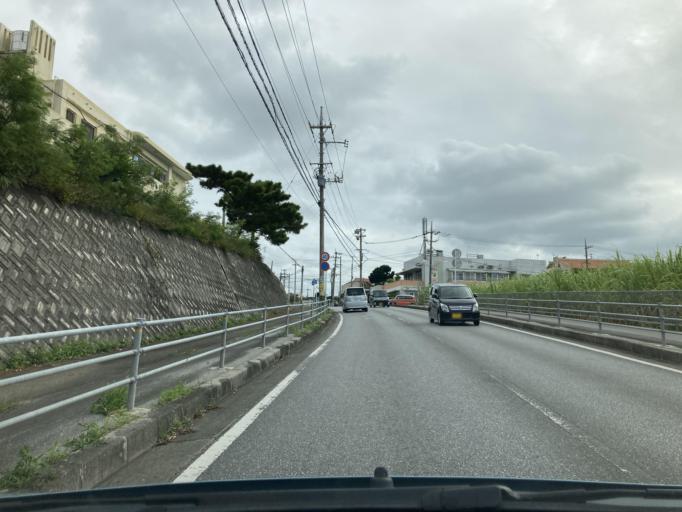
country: JP
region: Okinawa
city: Tomigusuku
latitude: 26.1622
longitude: 127.6798
